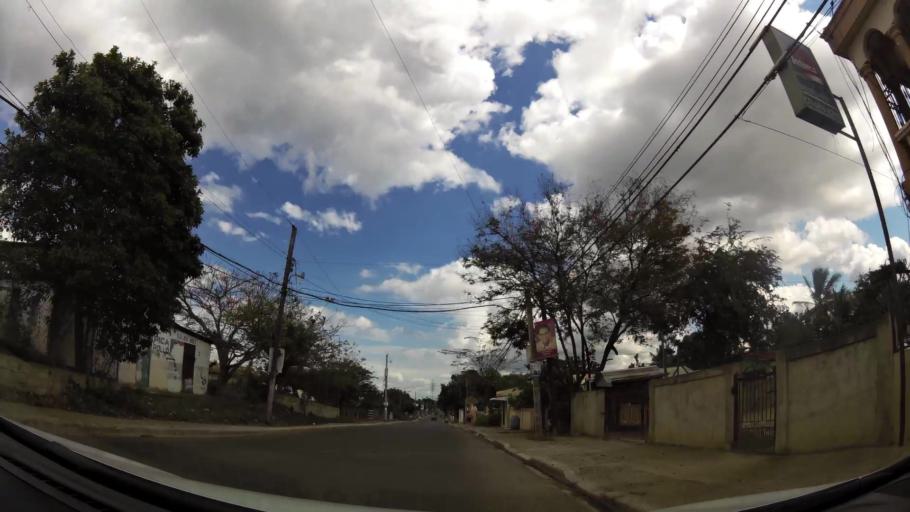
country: DO
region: Santiago
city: Santiago de los Caballeros
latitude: 19.4033
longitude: -70.6584
